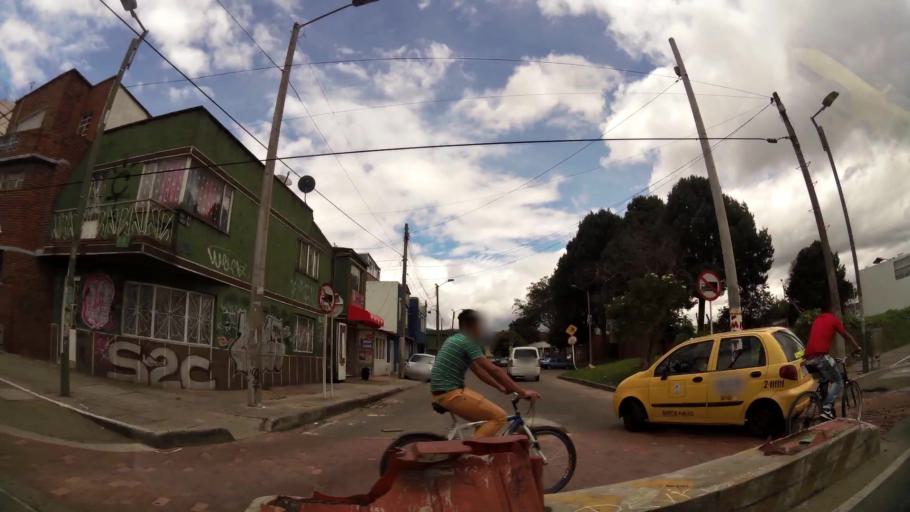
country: CO
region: Bogota D.C.
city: Barrio San Luis
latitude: 4.7051
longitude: -74.0993
